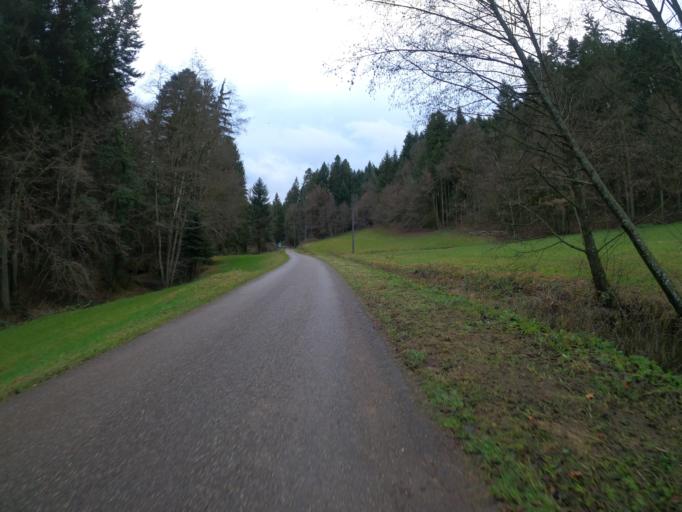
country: DE
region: Baden-Wuerttemberg
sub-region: Regierungsbezirk Stuttgart
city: Waschenbeuren
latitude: 48.7739
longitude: 9.7141
